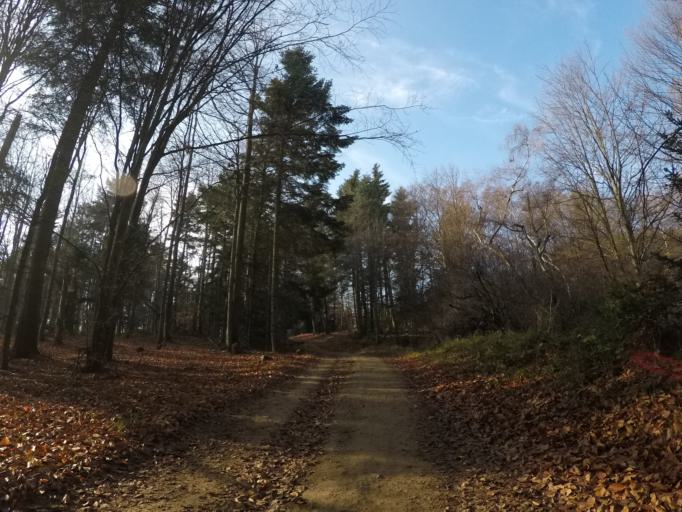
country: SK
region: Kosicky
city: Moldava nad Bodvou
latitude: 48.7640
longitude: 21.0811
